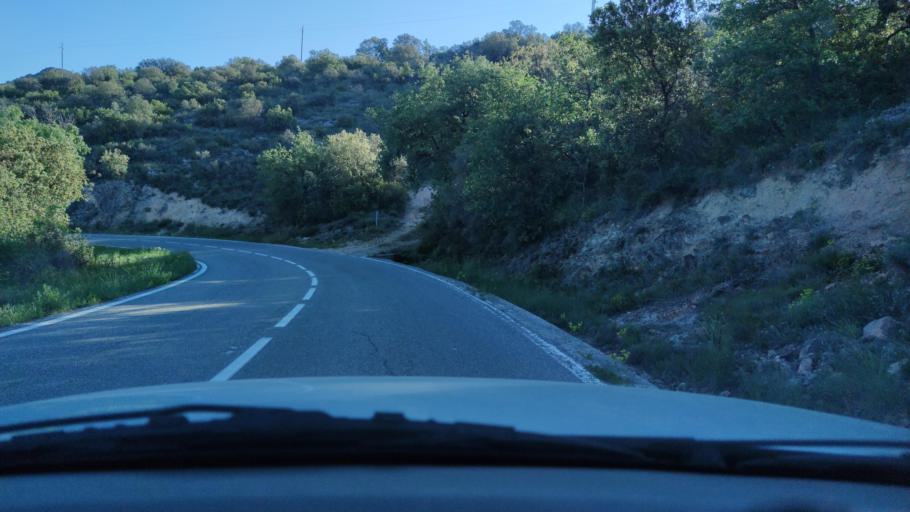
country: ES
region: Catalonia
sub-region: Provincia de Lleida
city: Artesa de Segre
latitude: 41.8807
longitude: 1.0073
